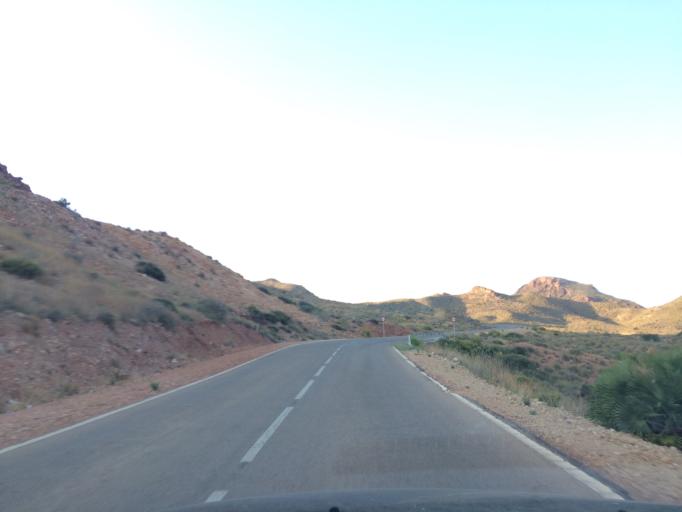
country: ES
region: Andalusia
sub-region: Provincia de Almeria
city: San Jose
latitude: 36.8616
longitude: -2.0278
